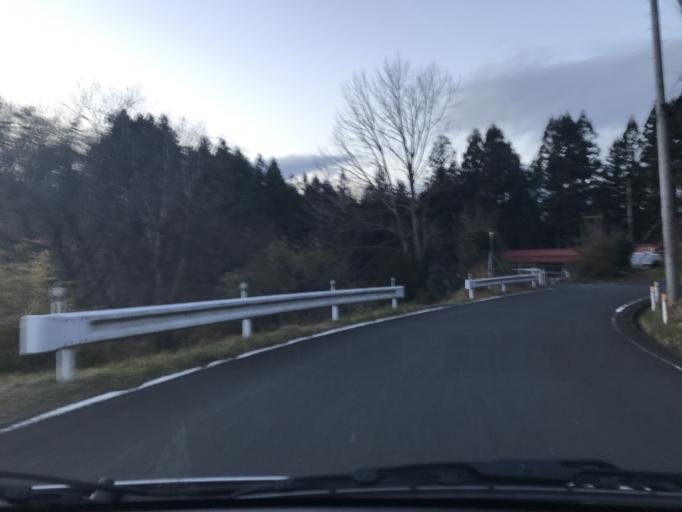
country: JP
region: Iwate
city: Ichinoseki
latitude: 38.8297
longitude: 141.0865
